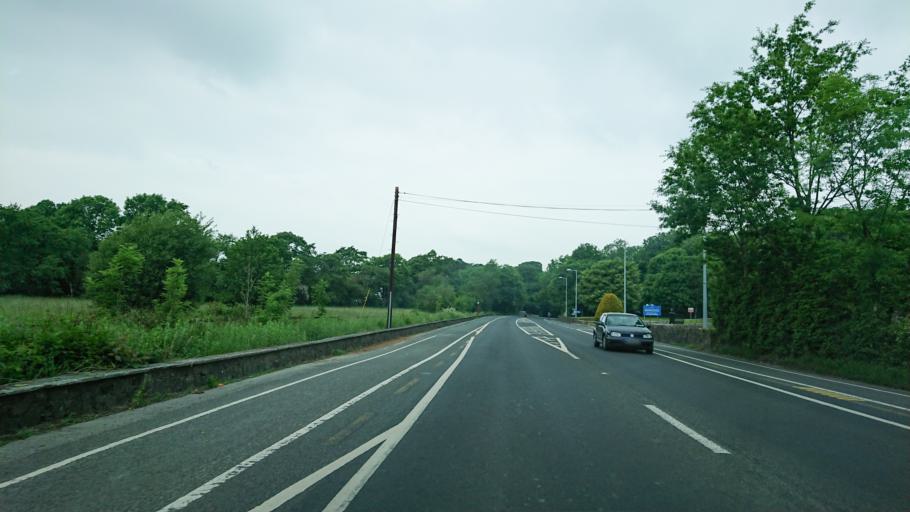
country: IE
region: Munster
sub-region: Waterford
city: Waterford
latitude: 52.2135
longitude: -7.1211
